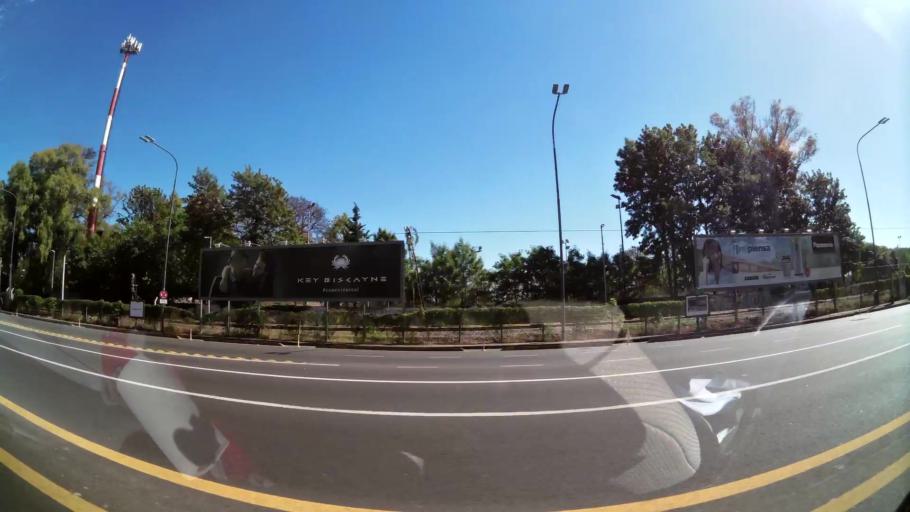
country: AR
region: Buenos Aires F.D.
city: Colegiales
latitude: -34.5627
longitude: -58.4394
